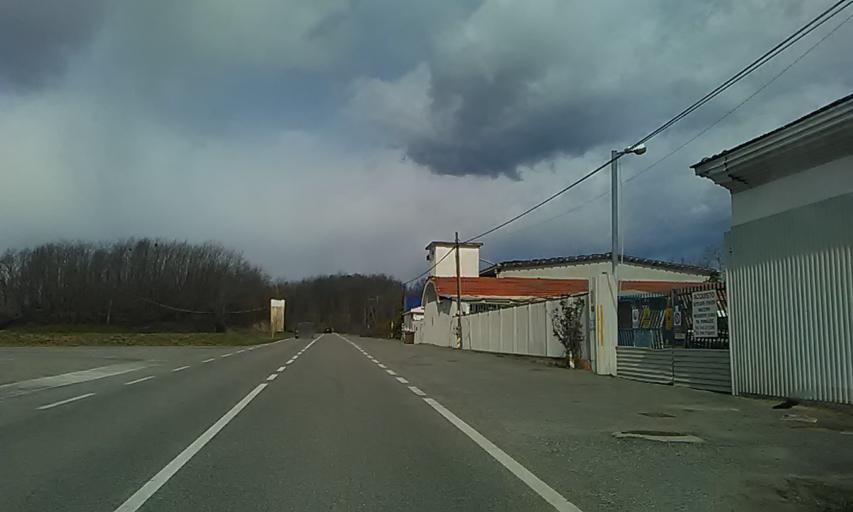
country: IT
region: Piedmont
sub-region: Provincia di Vercelli
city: Buronzo
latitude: 45.4943
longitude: 8.2565
